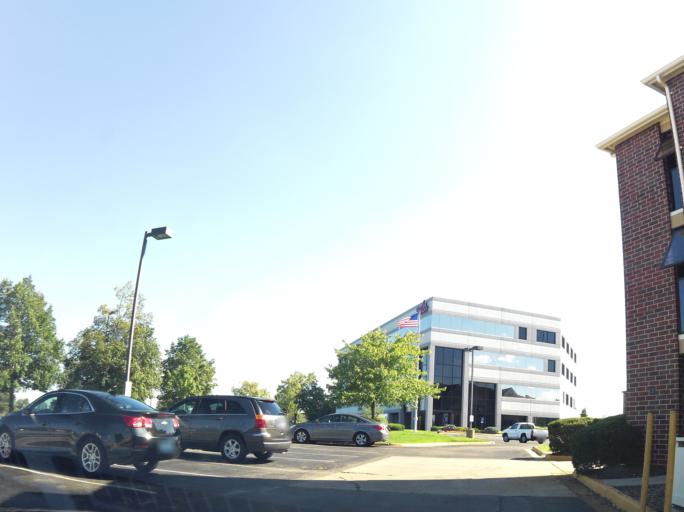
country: US
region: Ohio
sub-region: Greene County
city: Wright-Patterson AFB
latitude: 39.7770
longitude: -84.0557
